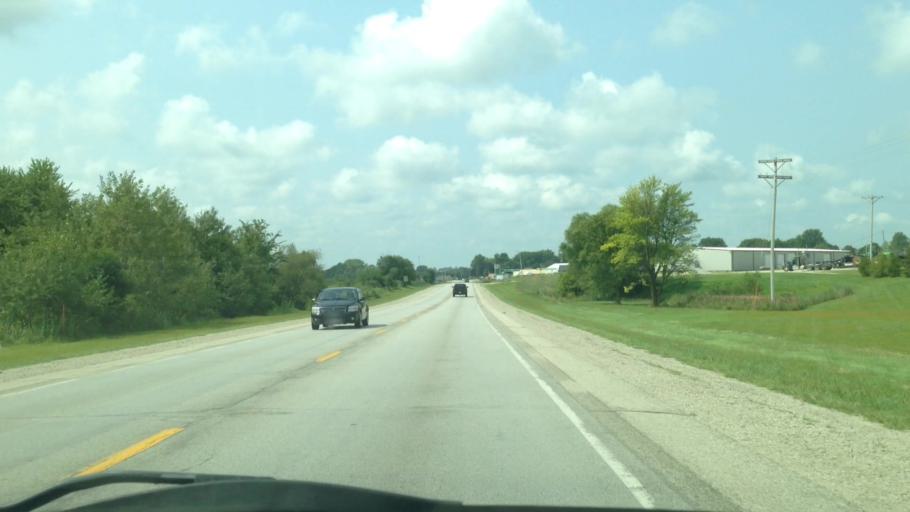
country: US
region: Iowa
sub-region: Benton County
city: Walford
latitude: 41.8841
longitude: -91.8254
